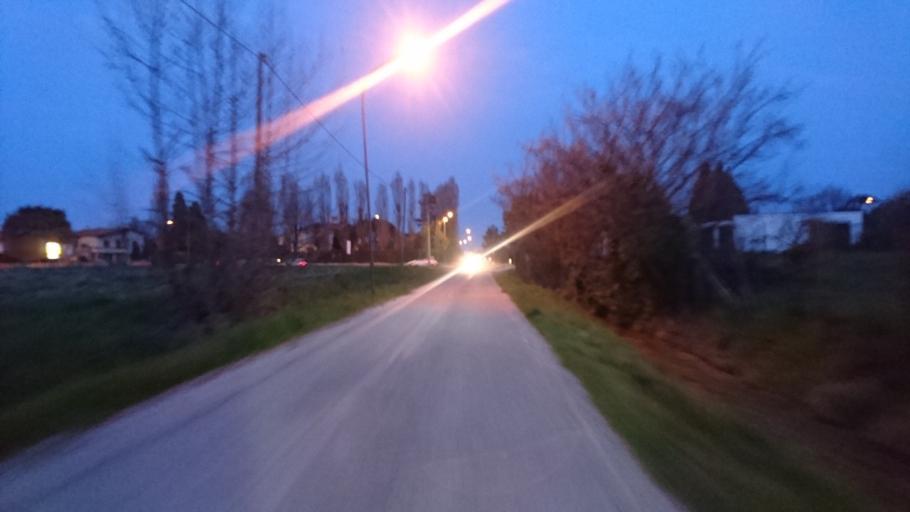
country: IT
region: Veneto
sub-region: Provincia di Padova
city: Selvazzano Dentro
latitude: 45.3730
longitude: 11.7910
